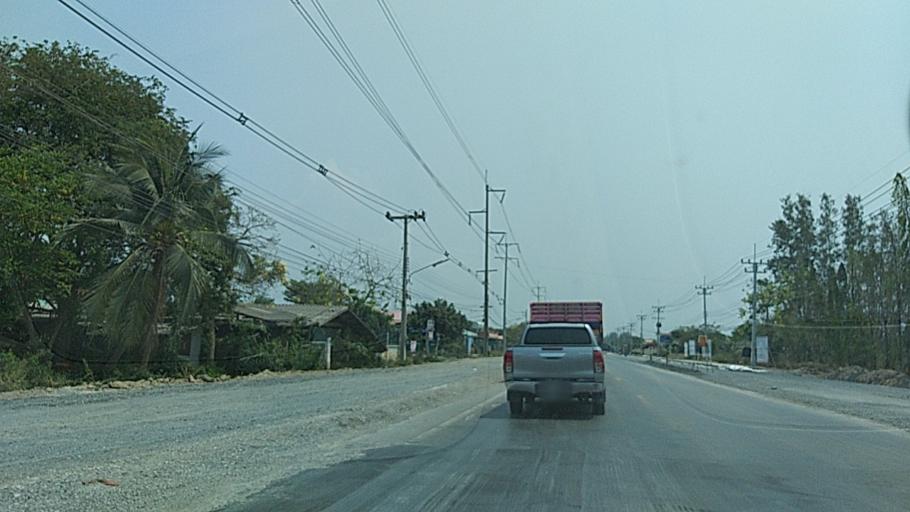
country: TH
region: Chachoengsao
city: Ban Pho
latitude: 13.5571
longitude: 101.1369
